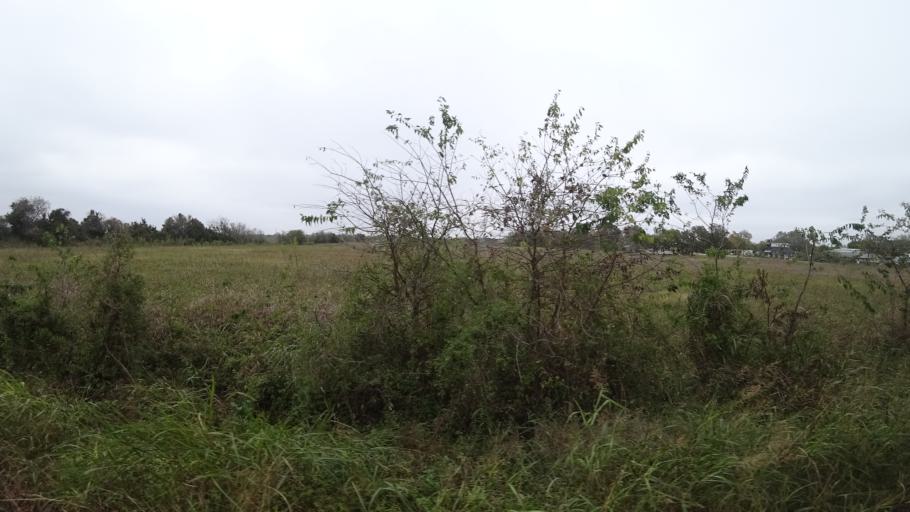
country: US
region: Texas
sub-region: Travis County
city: Pflugerville
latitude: 30.3741
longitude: -97.6253
